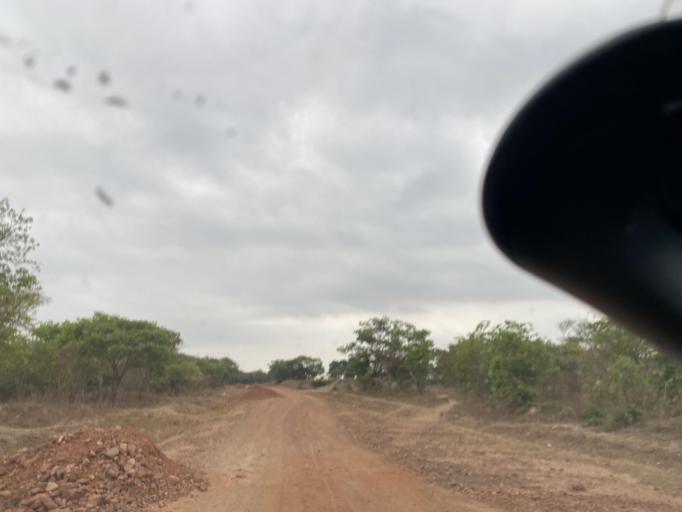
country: ZM
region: Lusaka
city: Chongwe
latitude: -15.1608
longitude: 28.7568
